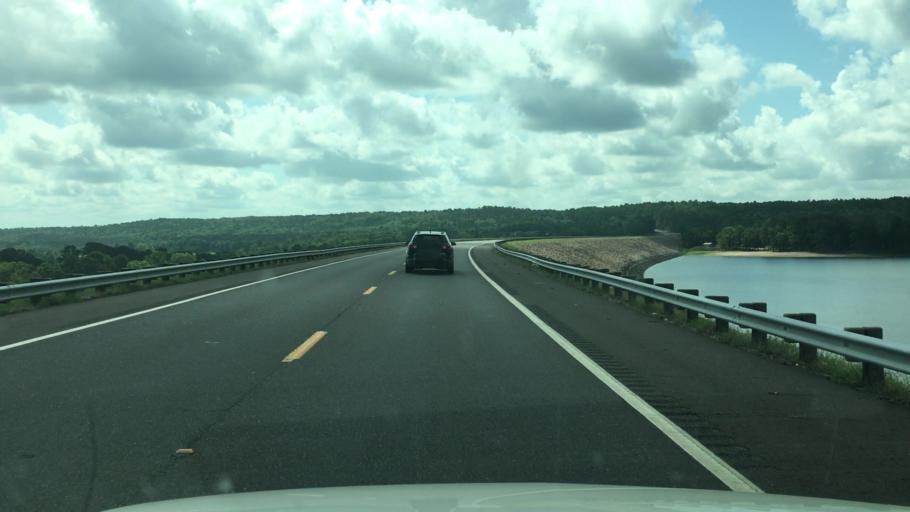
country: US
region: Arkansas
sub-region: Clark County
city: Arkadelphia
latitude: 34.2433
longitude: -93.1066
